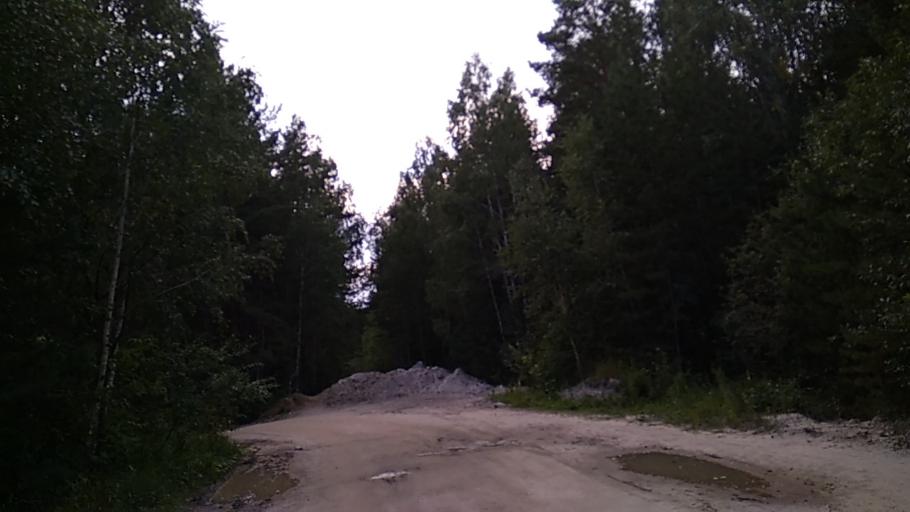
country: RU
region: Chelyabinsk
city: Kyshtym
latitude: 55.6768
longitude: 60.5910
